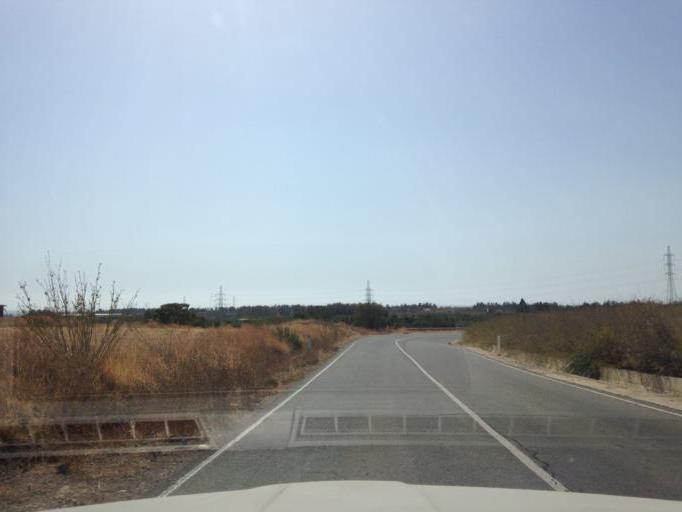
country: CY
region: Pafos
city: Mesogi
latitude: 34.7177
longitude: 32.5562
